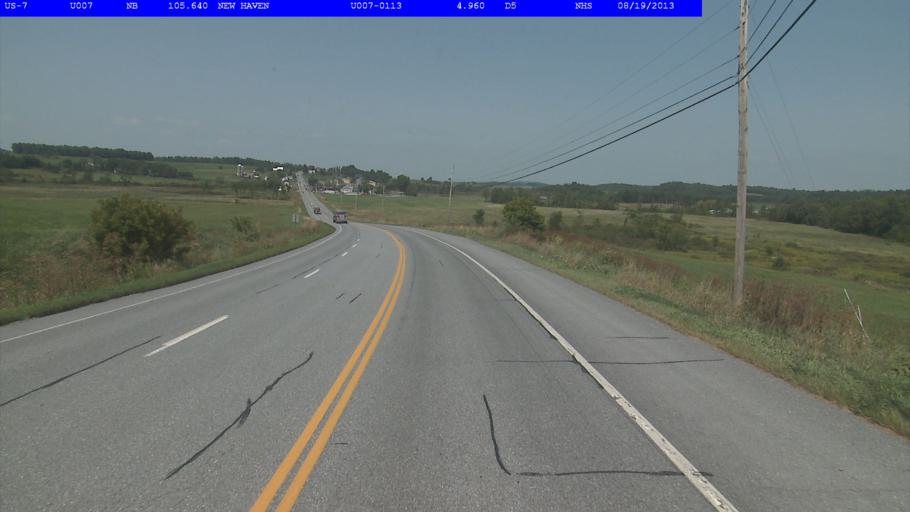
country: US
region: Vermont
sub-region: Addison County
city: Vergennes
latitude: 44.1166
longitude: -73.1766
